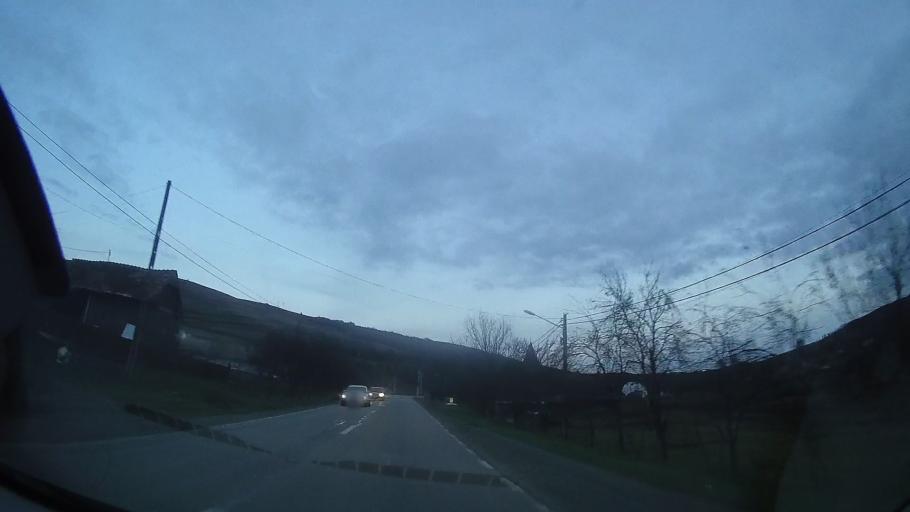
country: RO
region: Cluj
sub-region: Comuna Caianu
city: Vaida-Camaras
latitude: 46.8070
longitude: 23.9694
